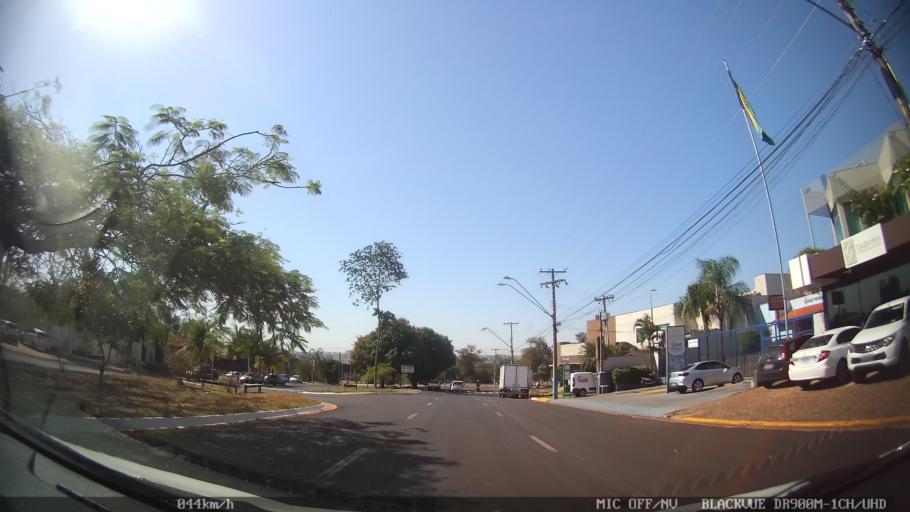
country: BR
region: Sao Paulo
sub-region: Ribeirao Preto
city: Ribeirao Preto
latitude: -21.2160
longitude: -47.7829
